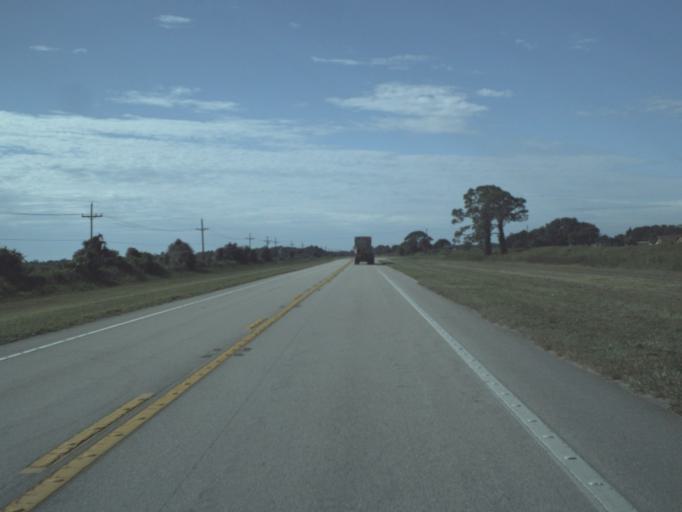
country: US
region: Florida
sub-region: Hendry County
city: Port LaBelle
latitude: 26.6401
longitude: -81.4363
